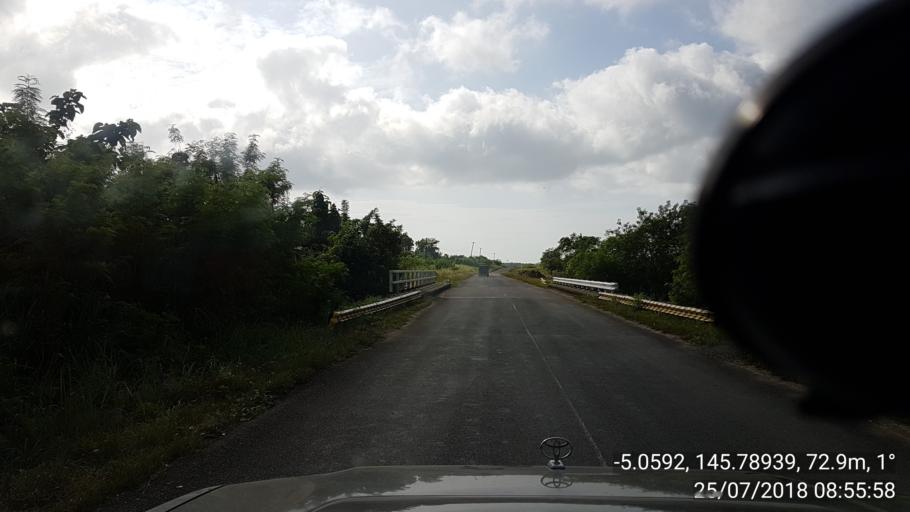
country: PG
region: Madang
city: Madang
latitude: -5.0592
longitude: 145.7892
